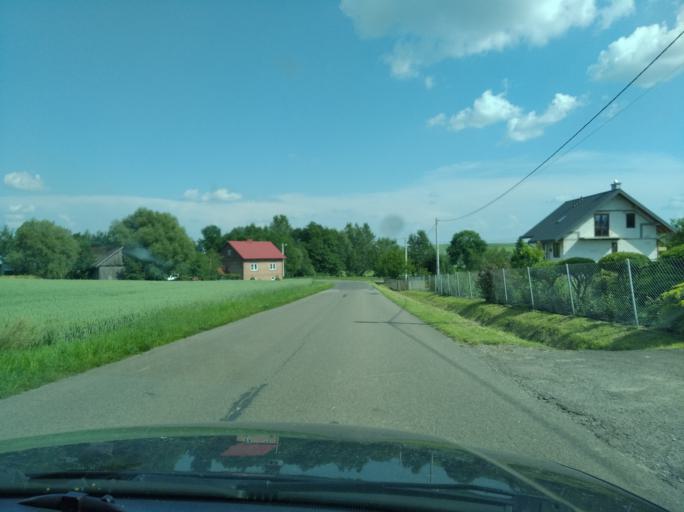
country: PL
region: Subcarpathian Voivodeship
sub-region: Powiat jaroslawski
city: Rokietnica
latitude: 49.9423
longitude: 22.6998
